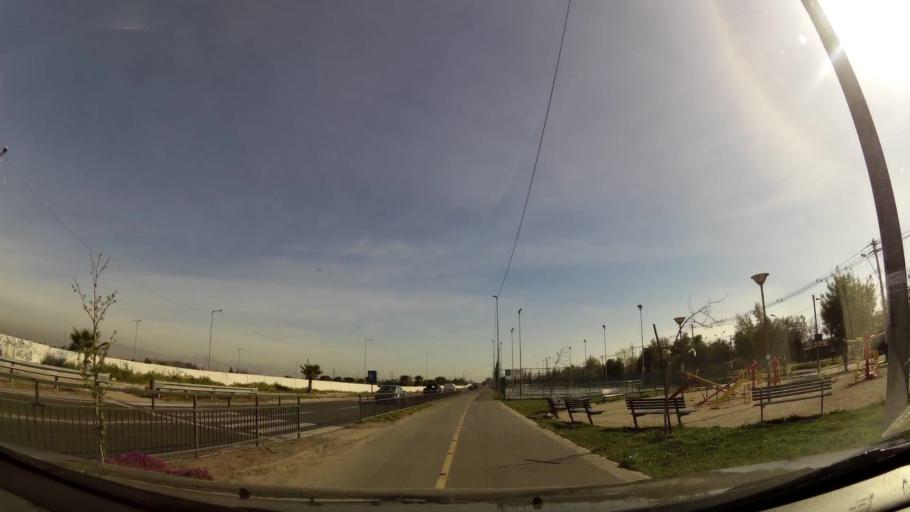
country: CL
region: Santiago Metropolitan
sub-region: Provincia de Cordillera
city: Puente Alto
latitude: -33.6098
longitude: -70.6027
